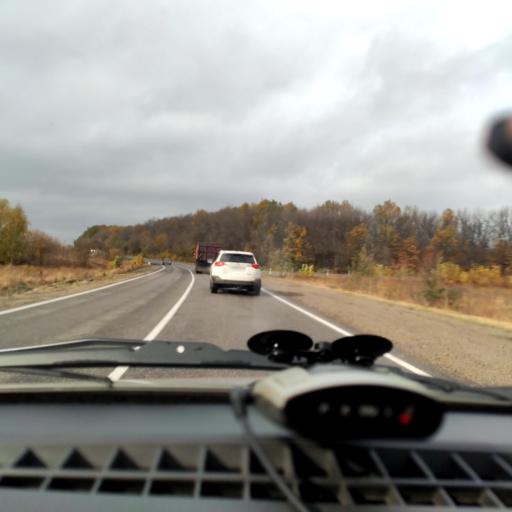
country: RU
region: Voronezj
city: Kolodeznyy
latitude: 51.3778
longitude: 39.0193
